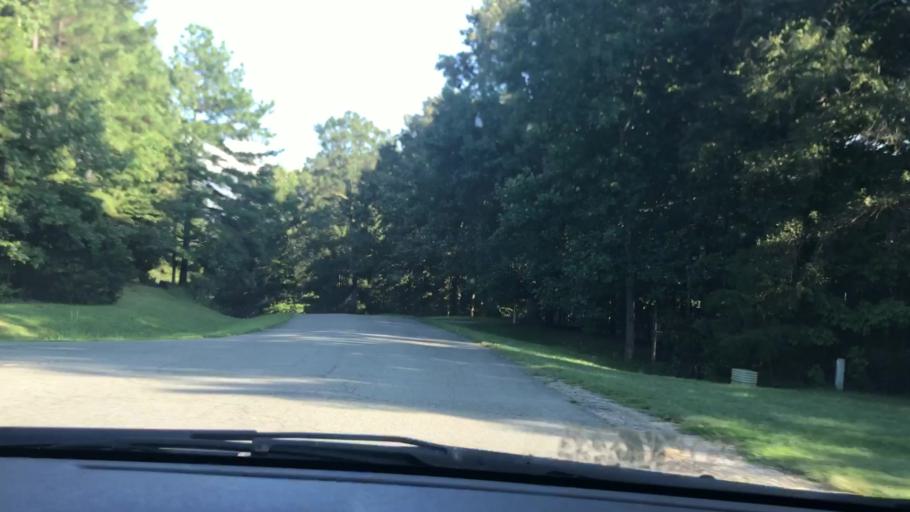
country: US
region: Virginia
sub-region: Henrico County
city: Short Pump
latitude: 37.6098
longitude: -77.7172
